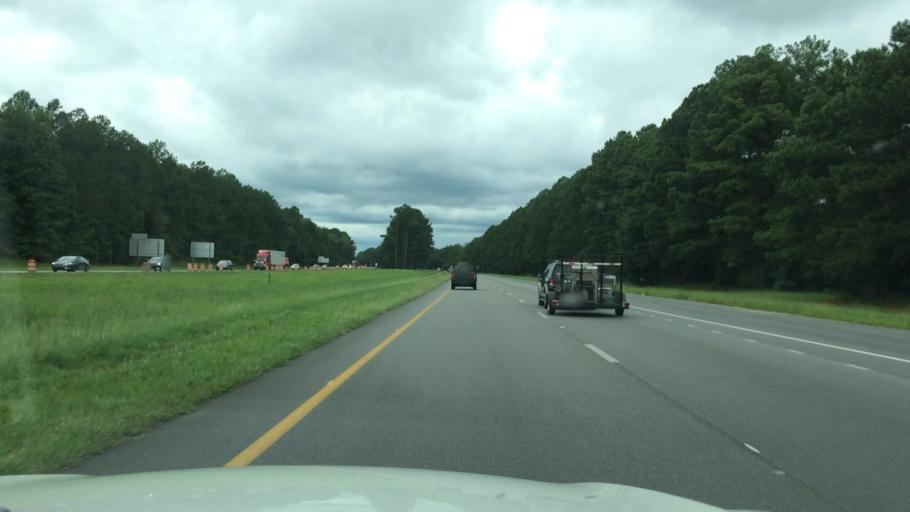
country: US
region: South Carolina
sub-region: Lee County
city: Bishopville
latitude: 34.1955
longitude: -80.2870
